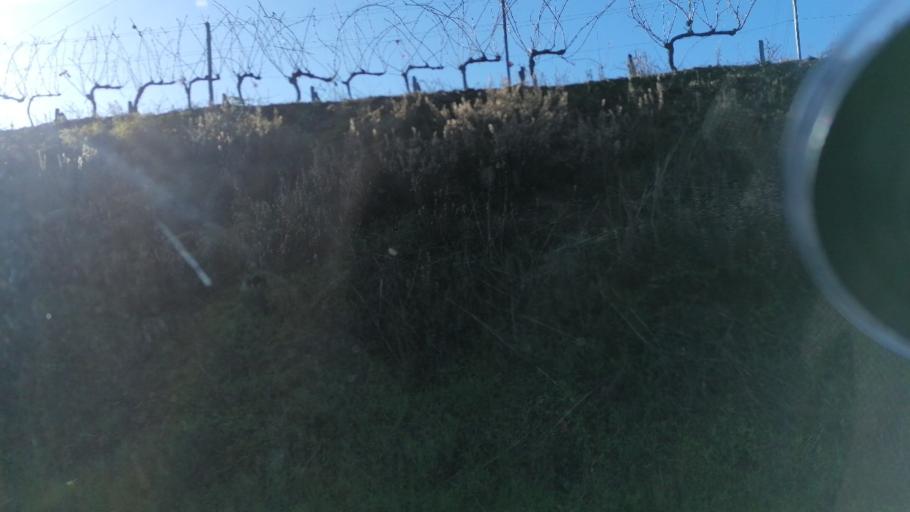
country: PT
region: Viseu
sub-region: Lamego
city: Lamego
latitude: 41.1169
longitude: -7.7898
